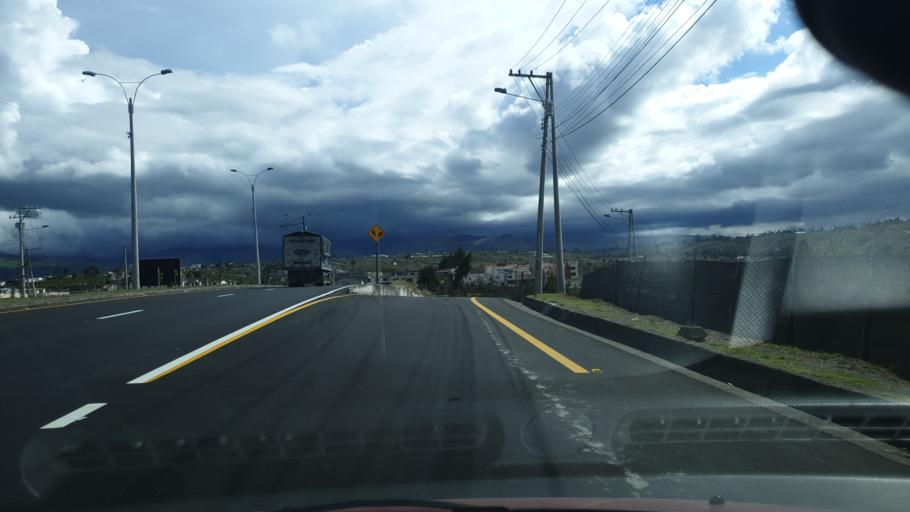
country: EC
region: Tungurahua
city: Ambato
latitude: -1.3027
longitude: -78.6360
